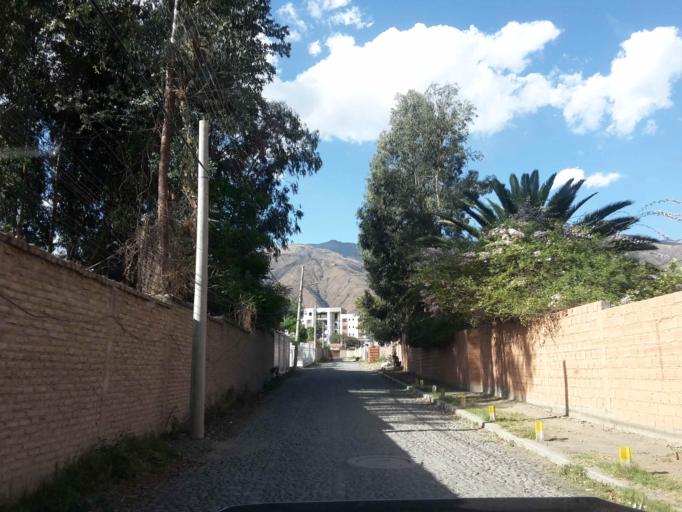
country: BO
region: Cochabamba
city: Cochabamba
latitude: -17.3551
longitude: -66.1998
